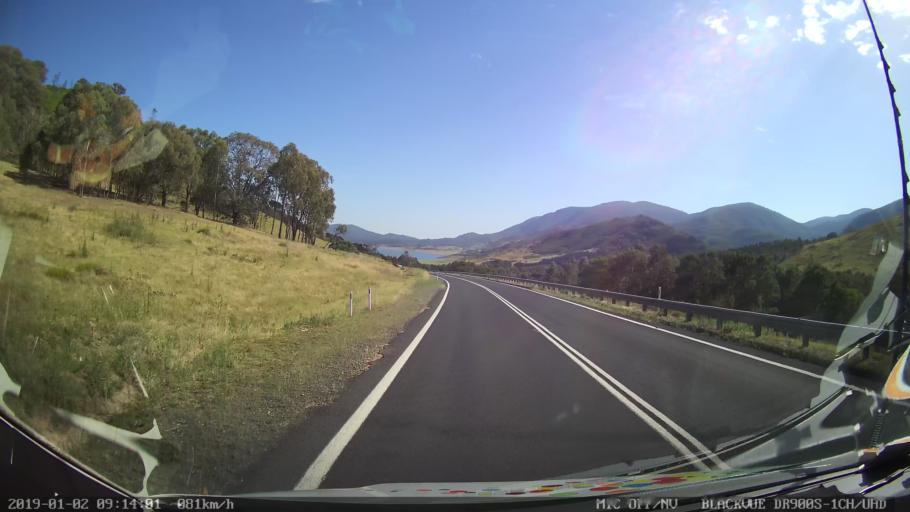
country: AU
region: New South Wales
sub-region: Tumut Shire
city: Tumut
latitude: -35.4825
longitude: 148.2722
